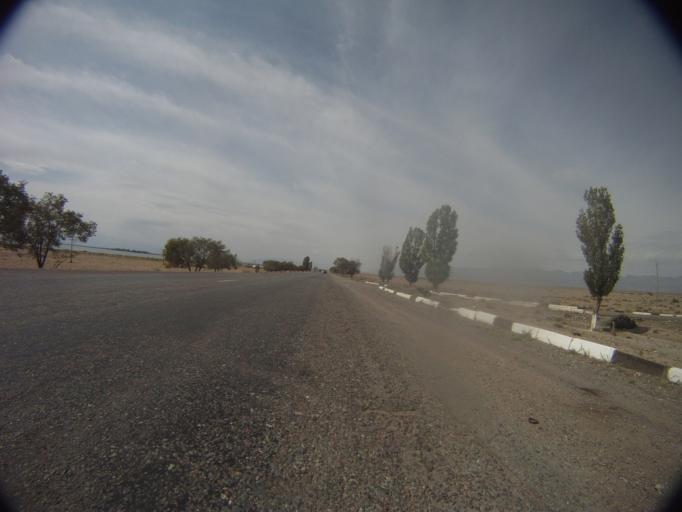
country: KG
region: Ysyk-Koel
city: Balykchy
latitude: 42.5106
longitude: 76.5068
